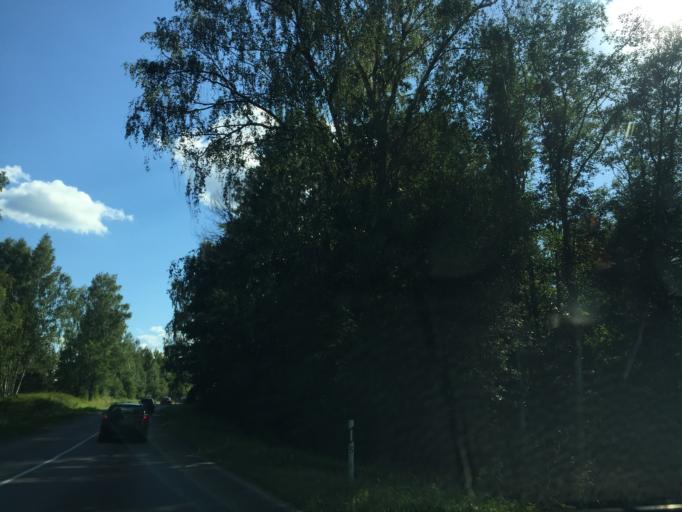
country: LV
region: Beverina
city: Murmuiza
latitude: 57.4262
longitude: 25.4389
